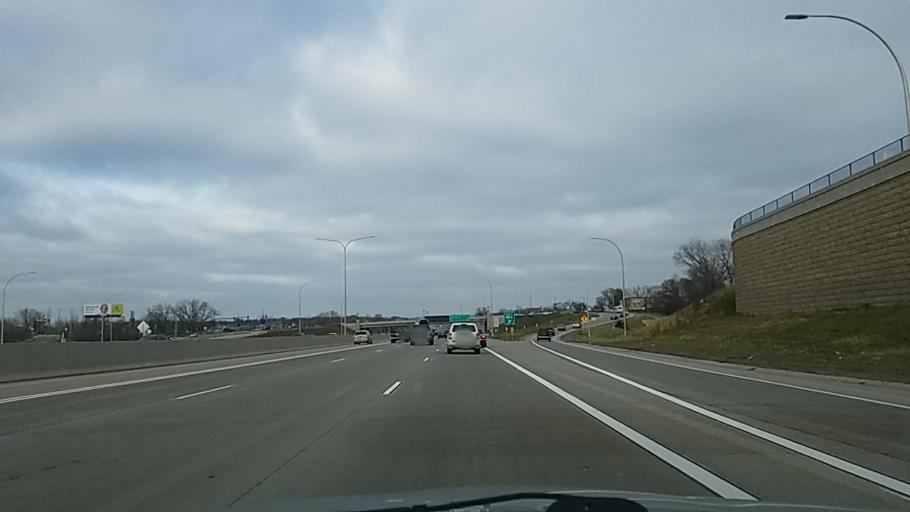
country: US
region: Minnesota
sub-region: Ramsey County
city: Saint Paul
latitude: 44.9740
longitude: -93.0884
